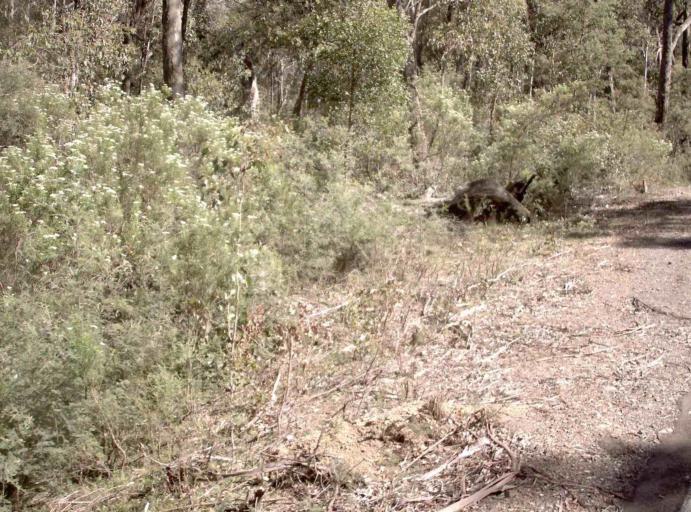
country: AU
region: New South Wales
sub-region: Bombala
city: Bombala
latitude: -37.1388
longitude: 148.7342
